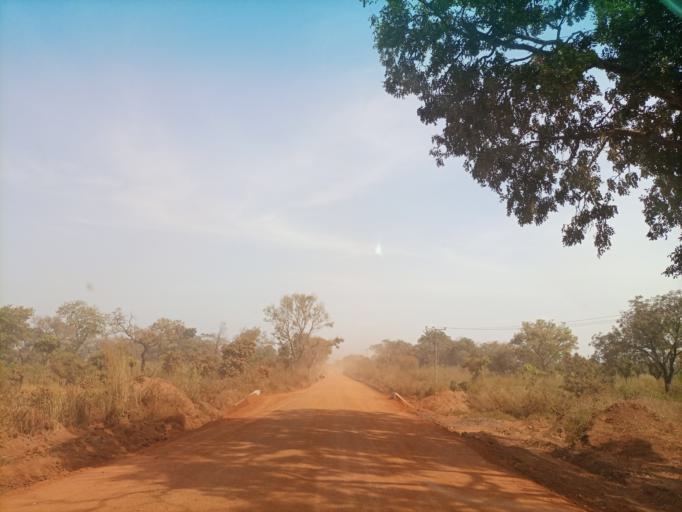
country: NG
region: Enugu
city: Eha Amufu
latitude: 6.6690
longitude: 7.7450
